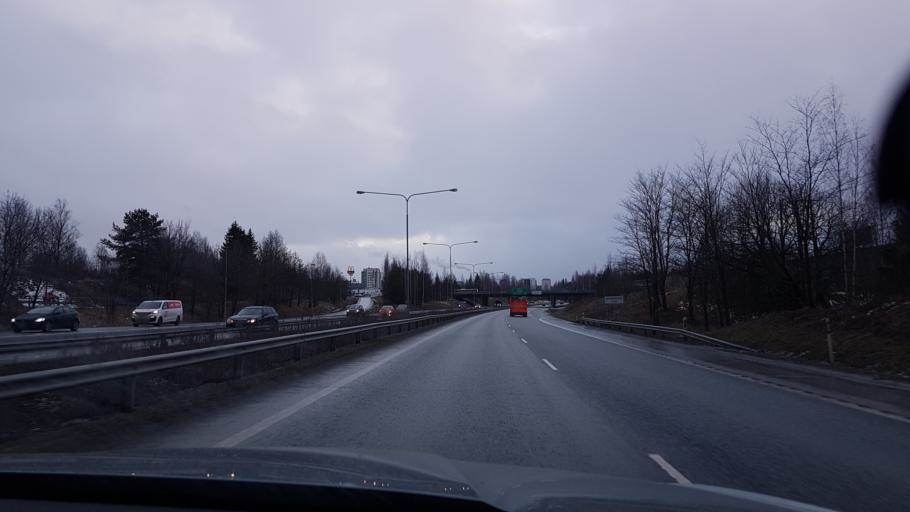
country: FI
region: Pirkanmaa
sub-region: Tampere
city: Tampere
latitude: 61.4812
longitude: 23.8725
